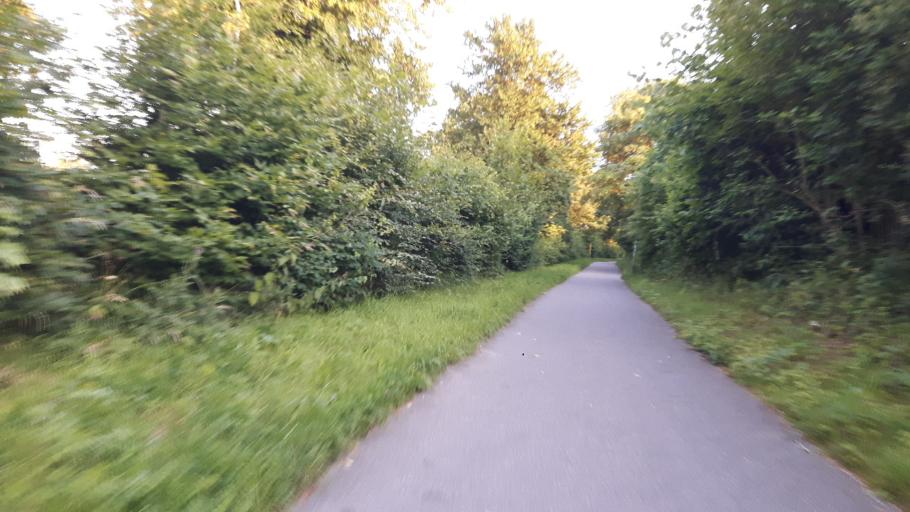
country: DE
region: Schleswig-Holstein
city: Travemuende
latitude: 53.9504
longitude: 10.8537
